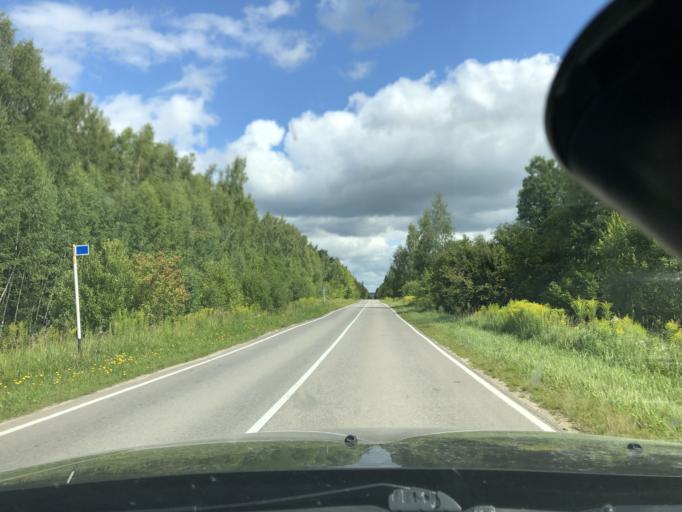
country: RU
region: Tula
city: Yasnogorsk
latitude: 54.4303
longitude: 37.6955
